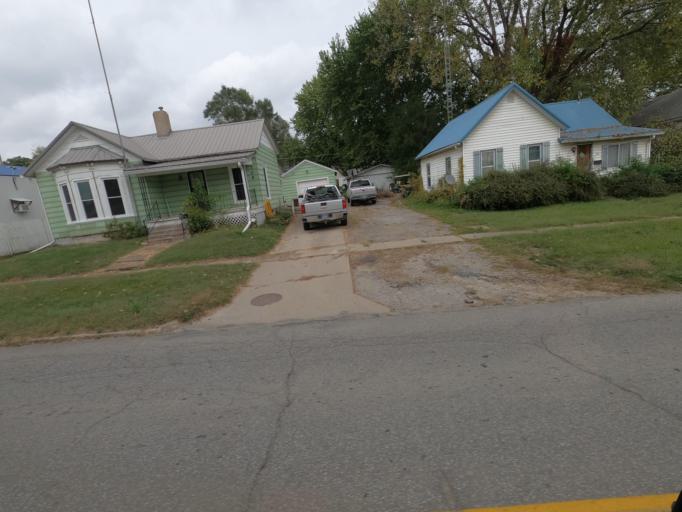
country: US
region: Iowa
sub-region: Wapello County
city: Ottumwa
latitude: 40.9205
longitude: -92.2265
